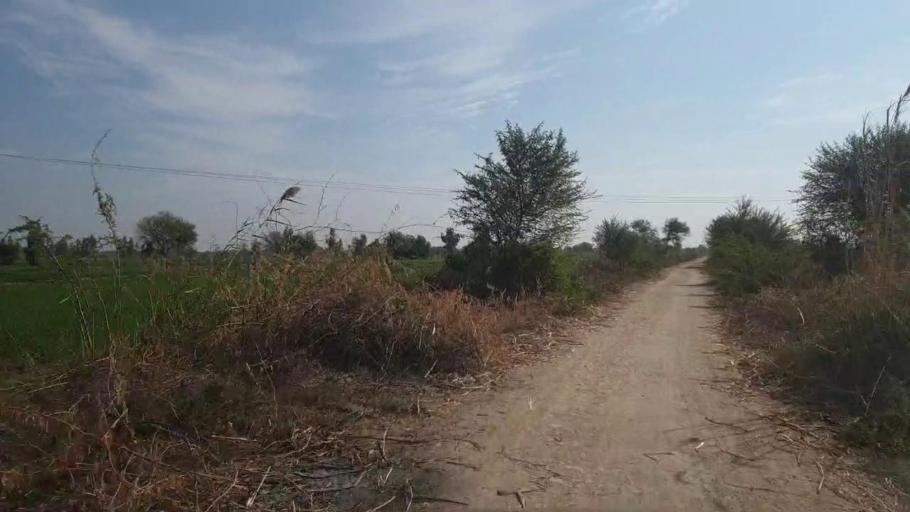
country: PK
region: Sindh
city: Mirwah Gorchani
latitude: 25.3652
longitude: 69.1928
